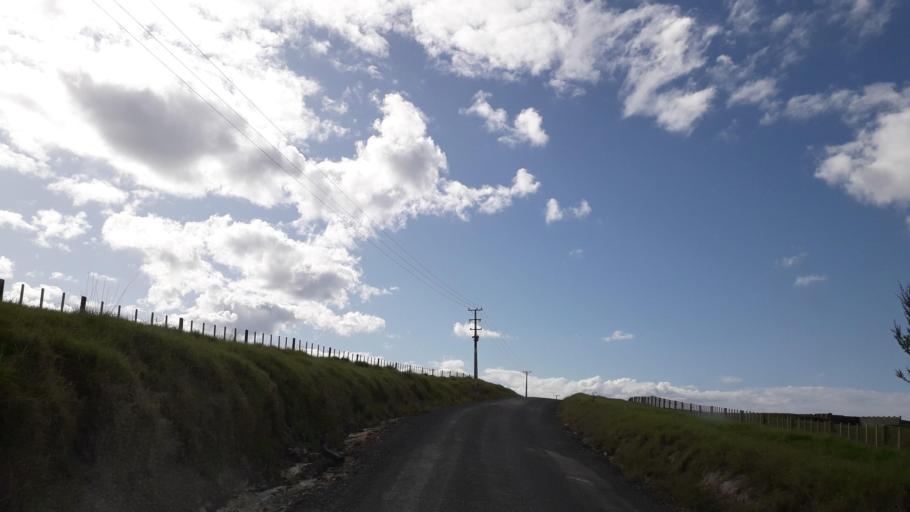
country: NZ
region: Northland
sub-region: Far North District
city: Kerikeri
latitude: -35.1465
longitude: 174.0377
